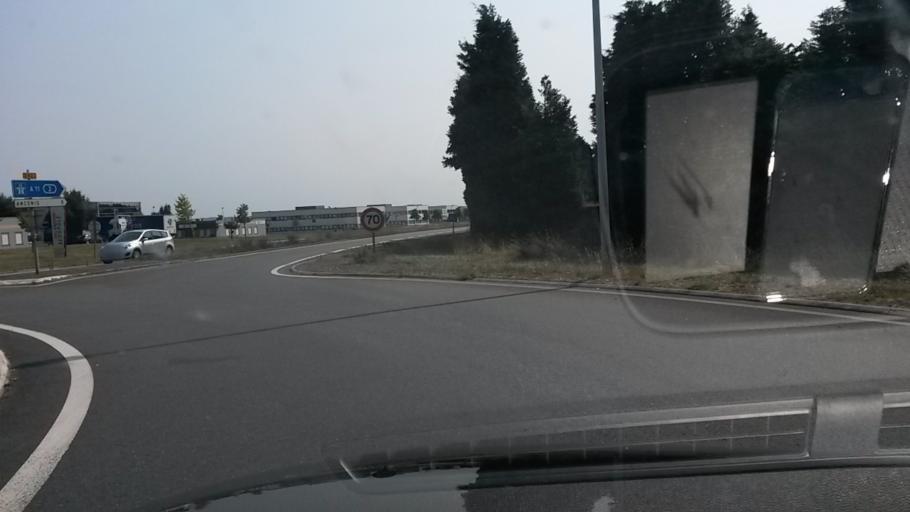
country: FR
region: Pays de la Loire
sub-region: Departement de la Loire-Atlantique
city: Mesanger
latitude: 47.4100
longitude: -1.1899
